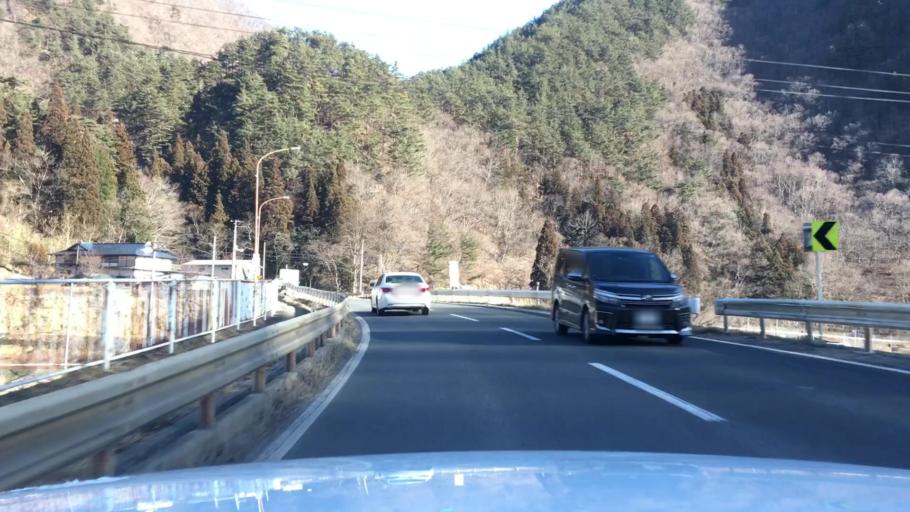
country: JP
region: Iwate
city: Miyako
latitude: 39.6108
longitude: 141.6451
